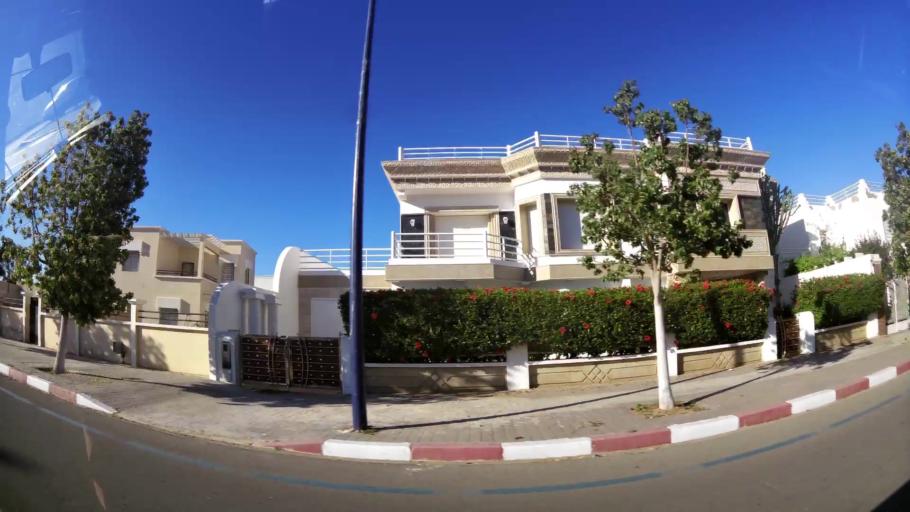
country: MA
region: Oriental
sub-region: Berkane-Taourirt
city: Madagh
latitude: 35.0924
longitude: -2.2563
